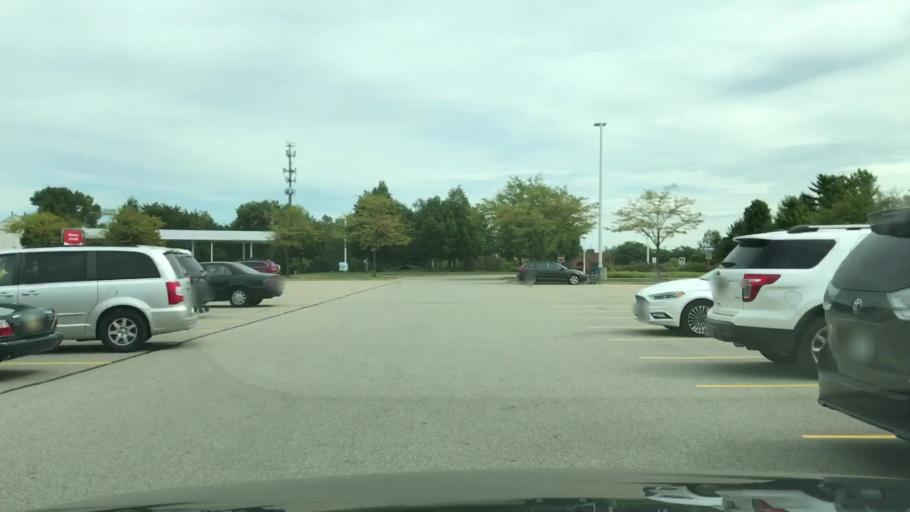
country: US
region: Michigan
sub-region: Kent County
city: Northview
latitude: 42.9965
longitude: -85.5928
